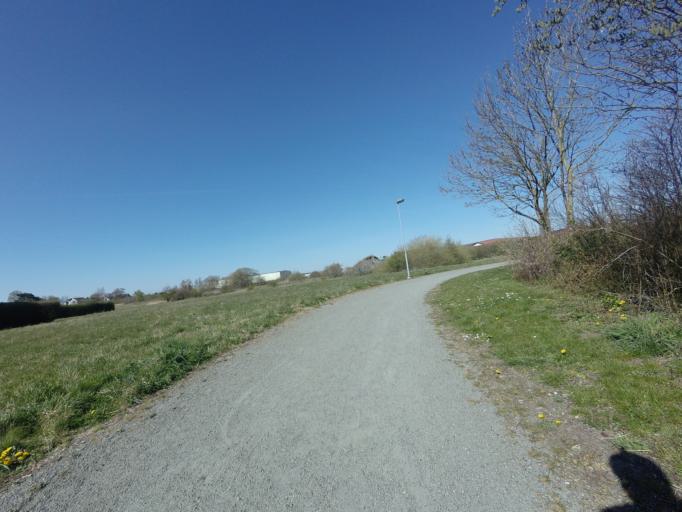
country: SE
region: Skane
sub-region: Trelleborgs Kommun
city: Trelleborg
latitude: 55.3787
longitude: 13.1164
